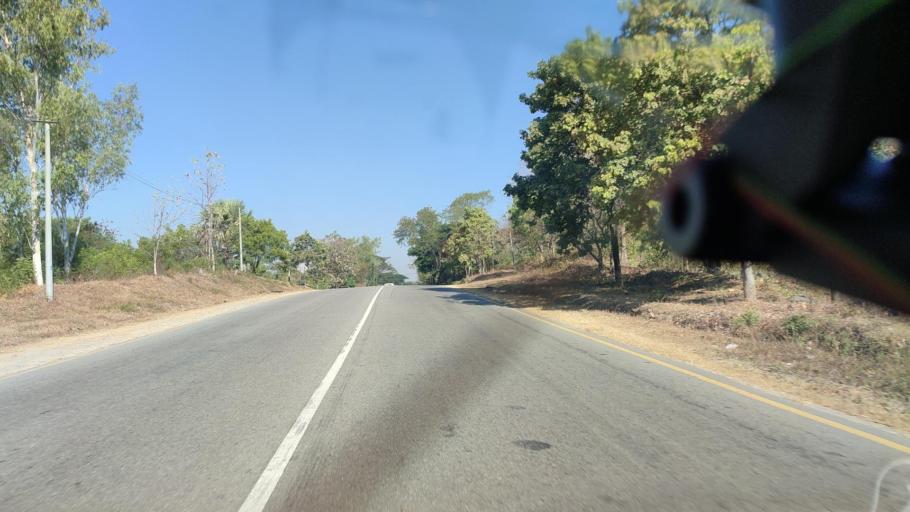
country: MM
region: Mandalay
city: Pyinmana
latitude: 19.8825
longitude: 96.2412
